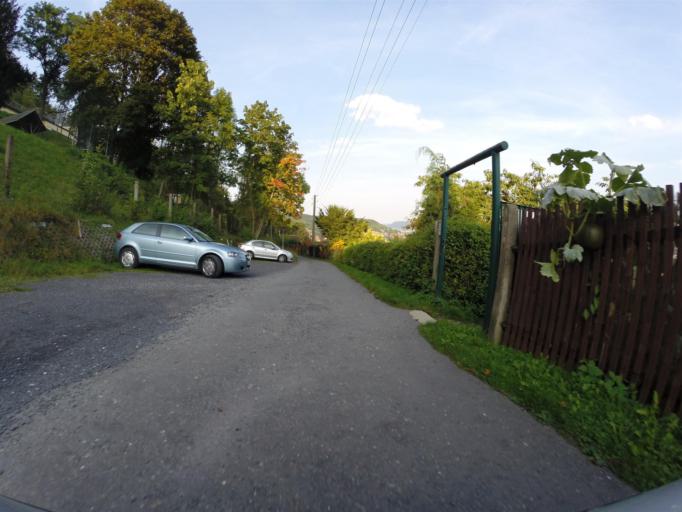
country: DE
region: Thuringia
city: Jena
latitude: 50.9283
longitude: 11.5618
